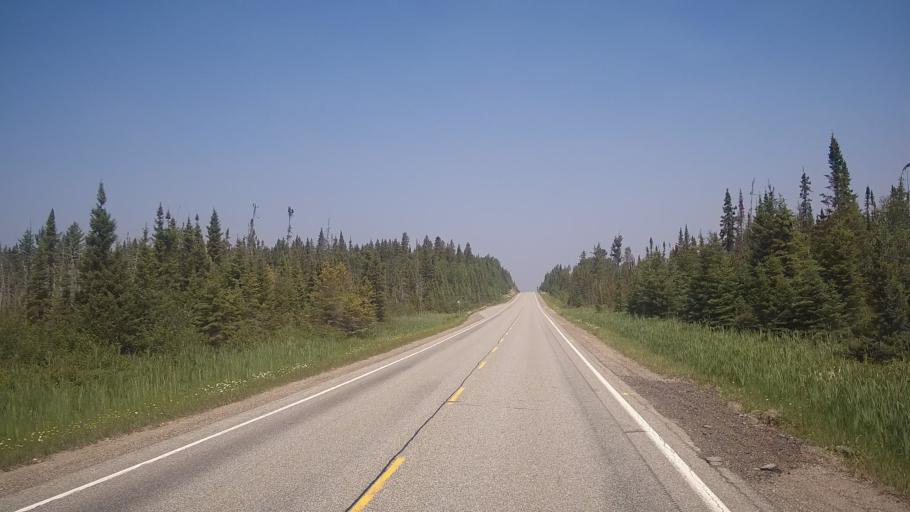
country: CA
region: Ontario
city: Timmins
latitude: 48.1776
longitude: -81.5824
